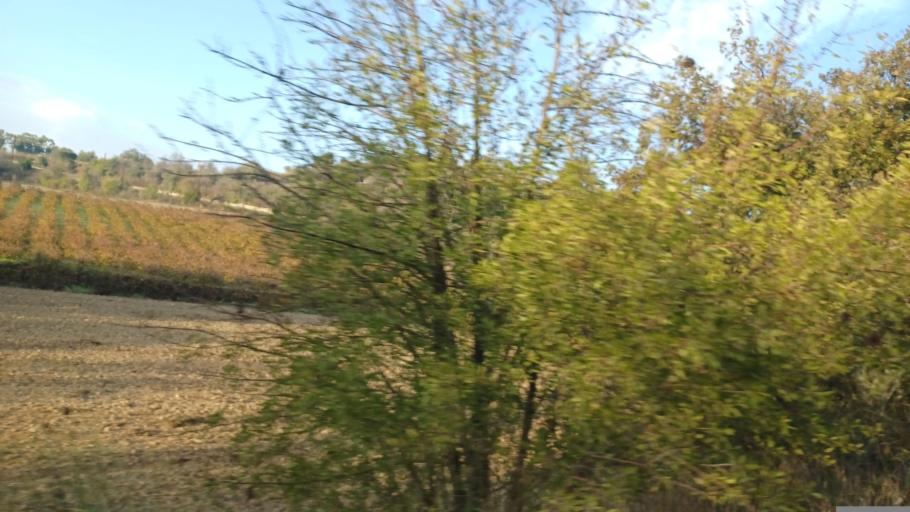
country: CY
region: Pafos
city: Tala
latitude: 34.8885
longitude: 32.4865
